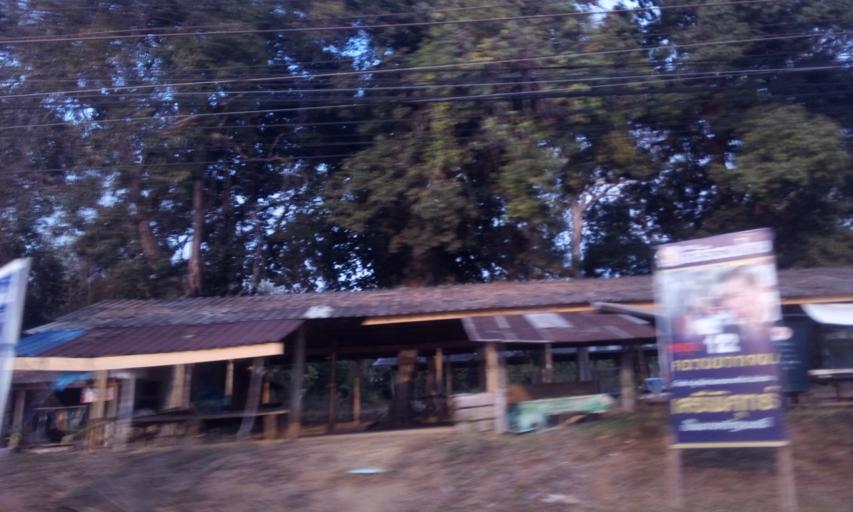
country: TH
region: Trat
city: Laem Ngop
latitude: 12.2554
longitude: 102.2877
